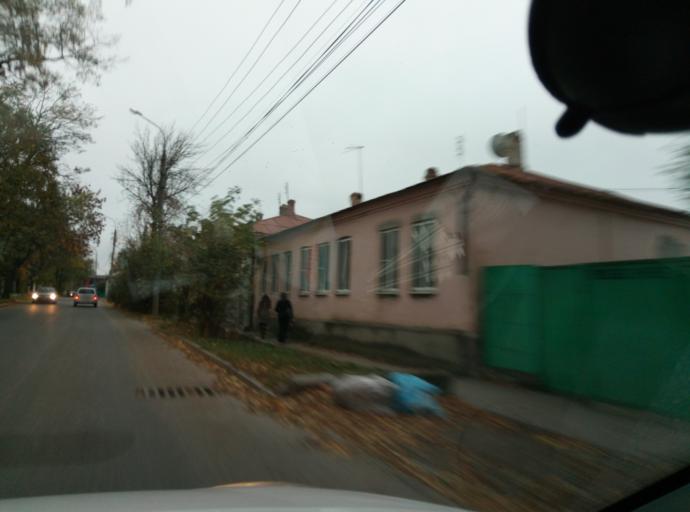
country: RU
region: Stavropol'skiy
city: Yessentuki
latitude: 44.0408
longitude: 42.8641
